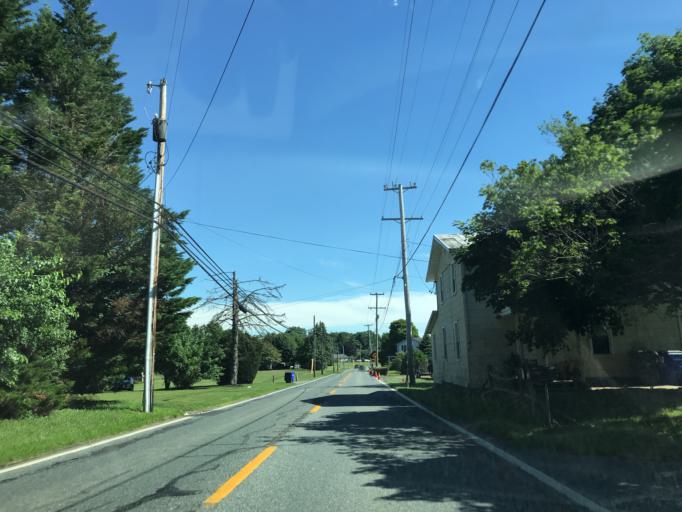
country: US
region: Maryland
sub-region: Harford County
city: Riverside
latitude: 39.5496
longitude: -76.2530
